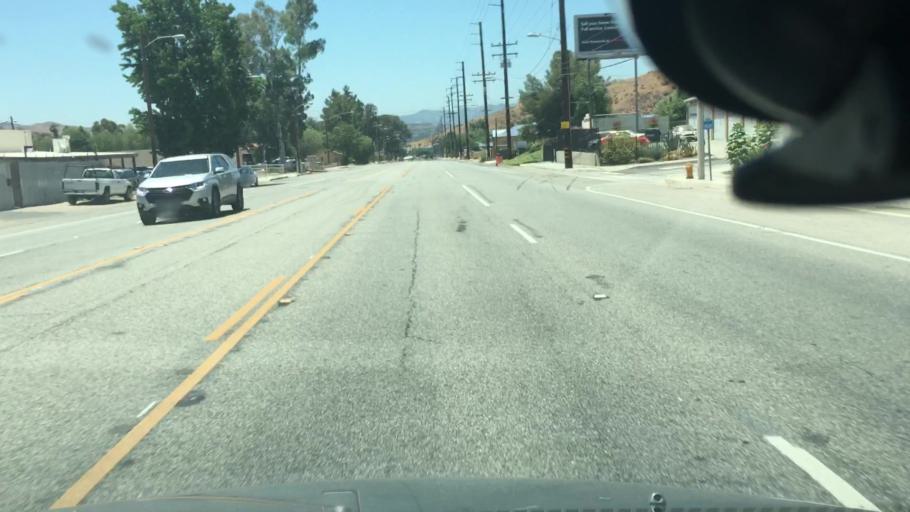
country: US
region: California
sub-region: Los Angeles County
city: Santa Clarita
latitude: 34.4281
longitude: -118.4460
